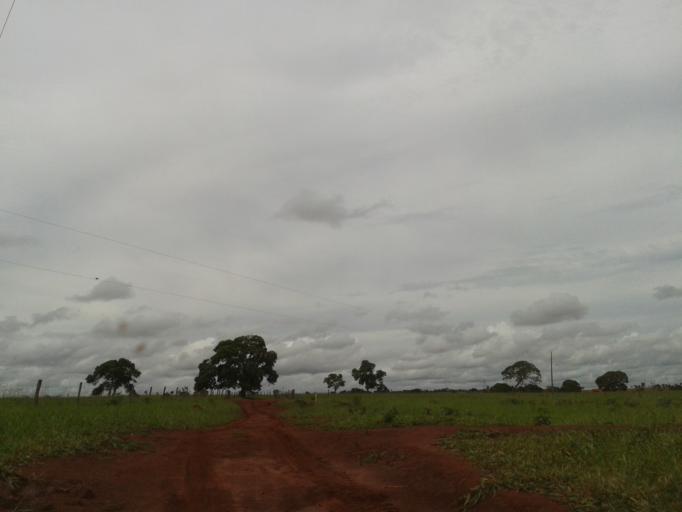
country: BR
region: Minas Gerais
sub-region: Capinopolis
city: Capinopolis
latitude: -18.7801
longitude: -49.7826
